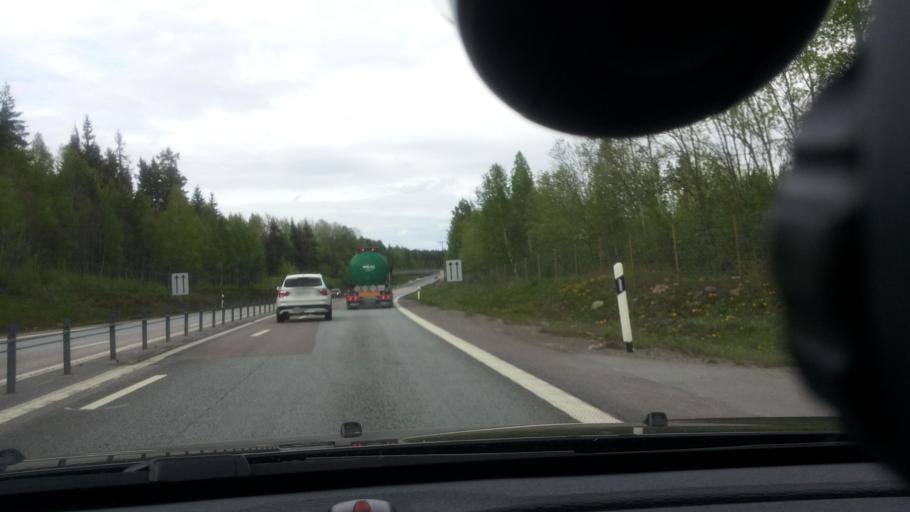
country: SE
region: Gaevleborg
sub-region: Gavle Kommun
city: Norrsundet
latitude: 60.9298
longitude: 17.0102
